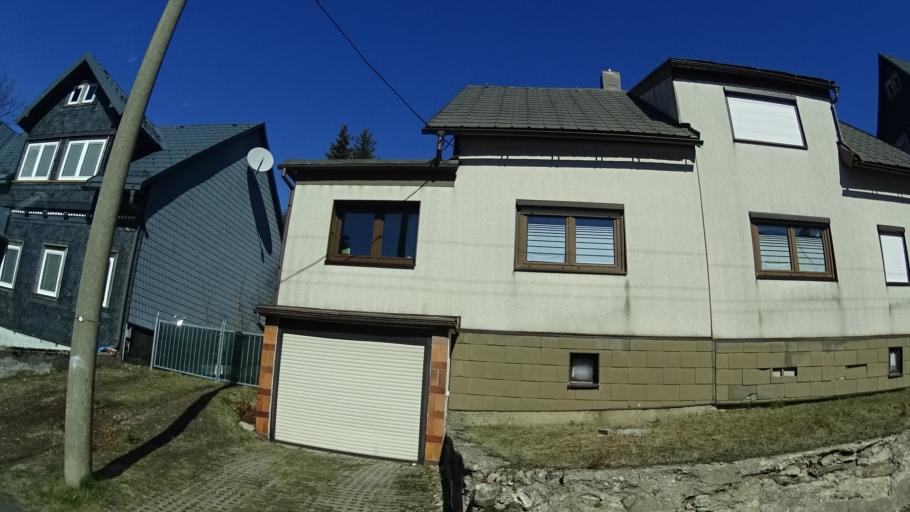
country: DE
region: Thuringia
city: Steinheid
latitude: 50.4639
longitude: 11.0849
